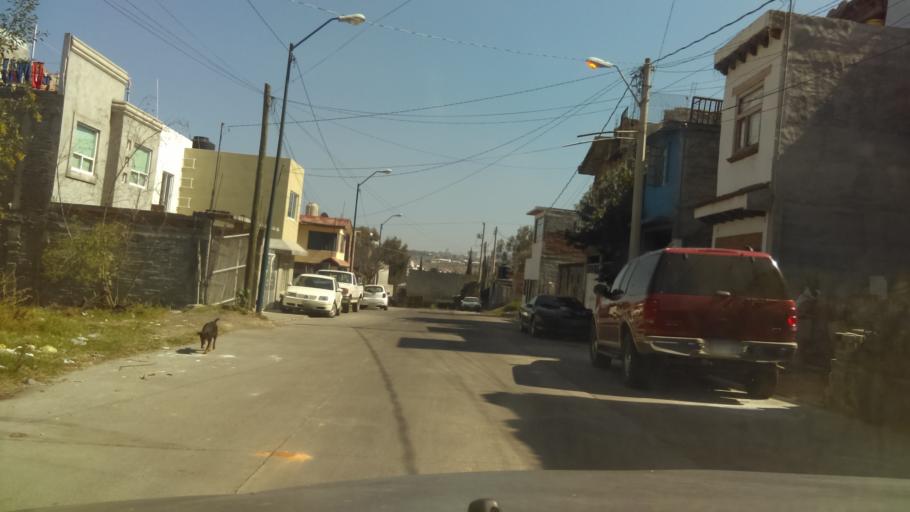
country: MX
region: Michoacan
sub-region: Morelia
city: Montana Monarca (Punta Altozano)
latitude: 19.6651
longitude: -101.1852
